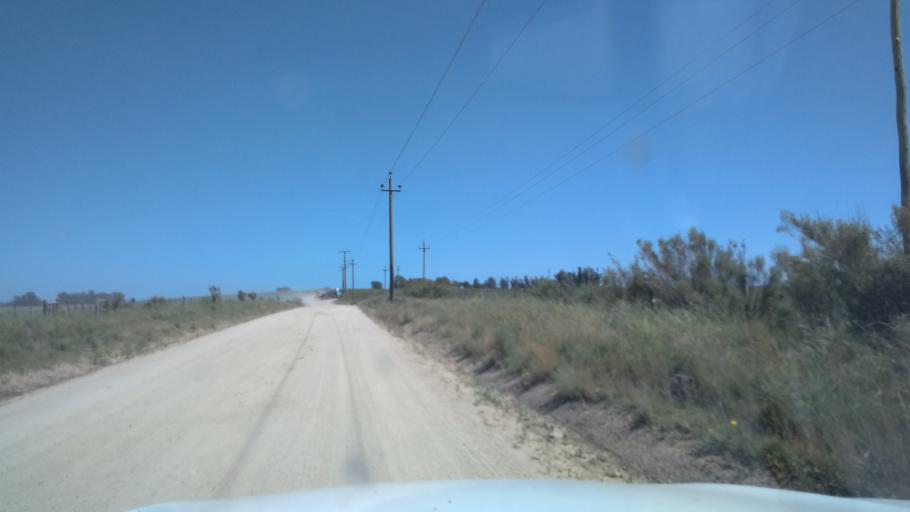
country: UY
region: Florida
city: Casupa
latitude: -34.0519
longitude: -55.8948
